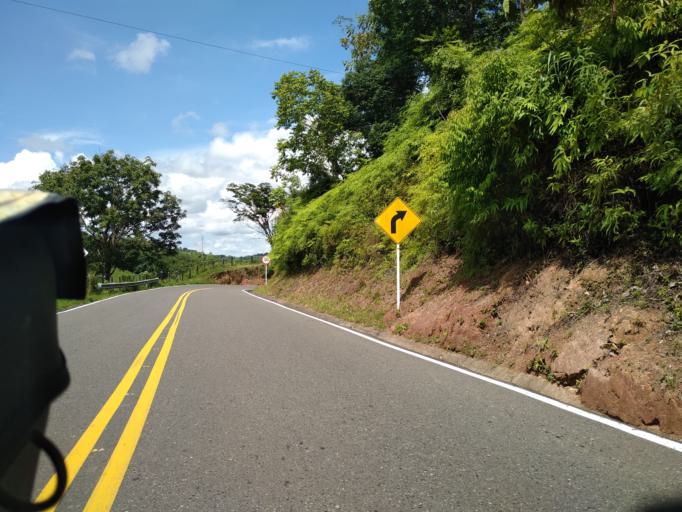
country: CO
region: Santander
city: Cimitarra
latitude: 6.4456
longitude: -74.0196
